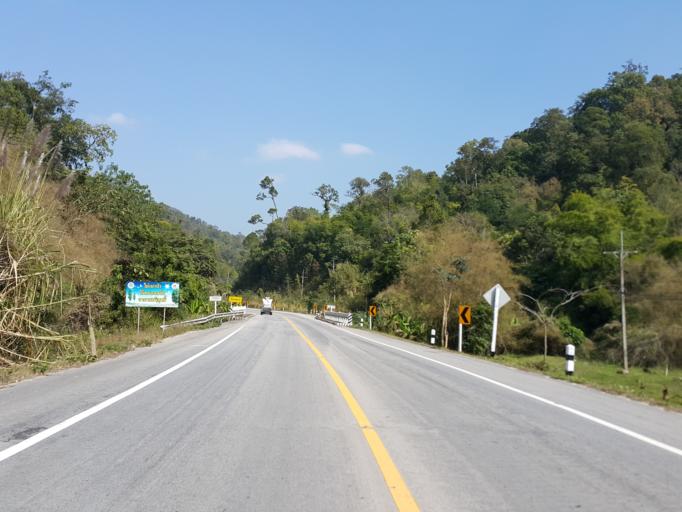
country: TH
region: Lampang
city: Wang Nuea
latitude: 19.0895
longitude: 99.4176
